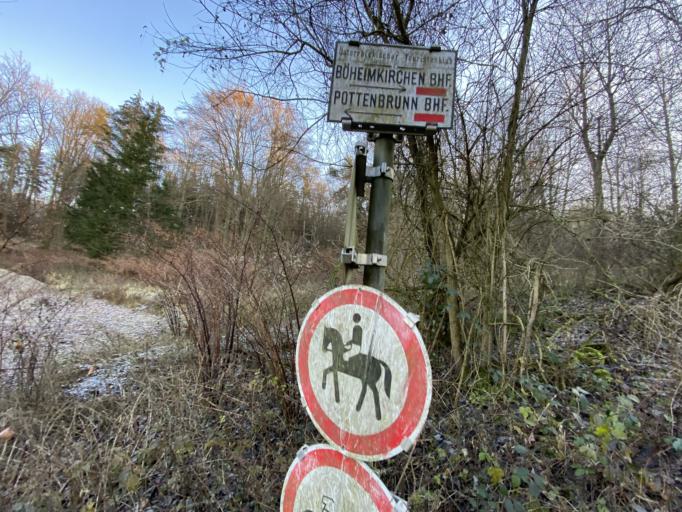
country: AT
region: Lower Austria
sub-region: Politischer Bezirk Sankt Polten
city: Boheimkirchen
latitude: 48.2192
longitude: 15.7107
